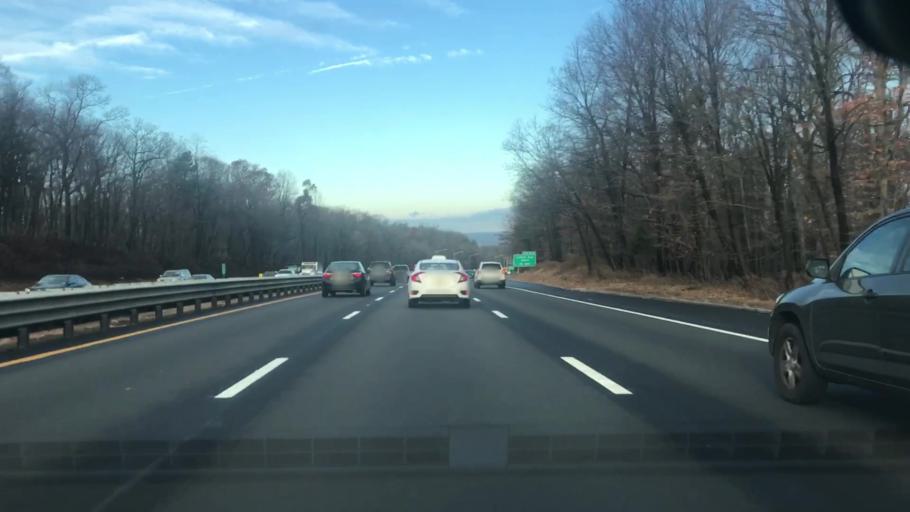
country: US
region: New Jersey
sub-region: Essex County
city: Essex Fells
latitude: 40.8022
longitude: -74.2800
